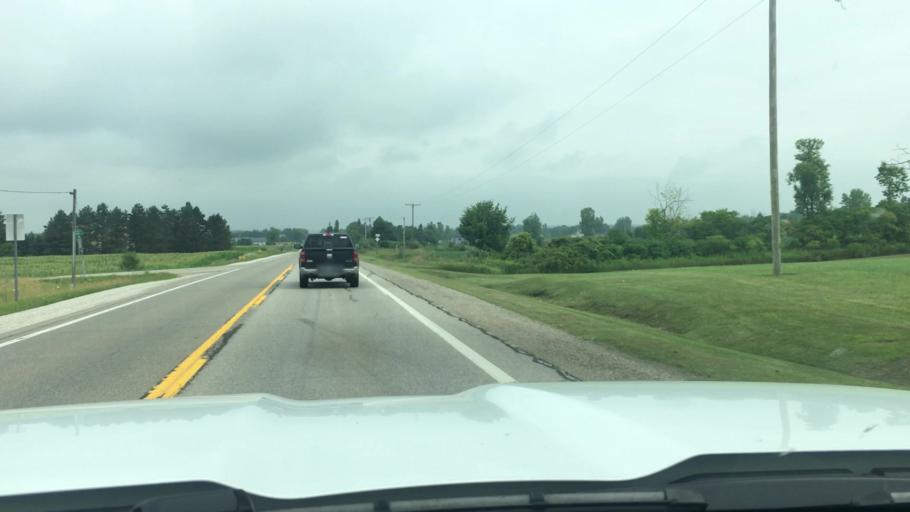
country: US
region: Michigan
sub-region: Sanilac County
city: Brown City
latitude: 43.1883
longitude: -83.0765
